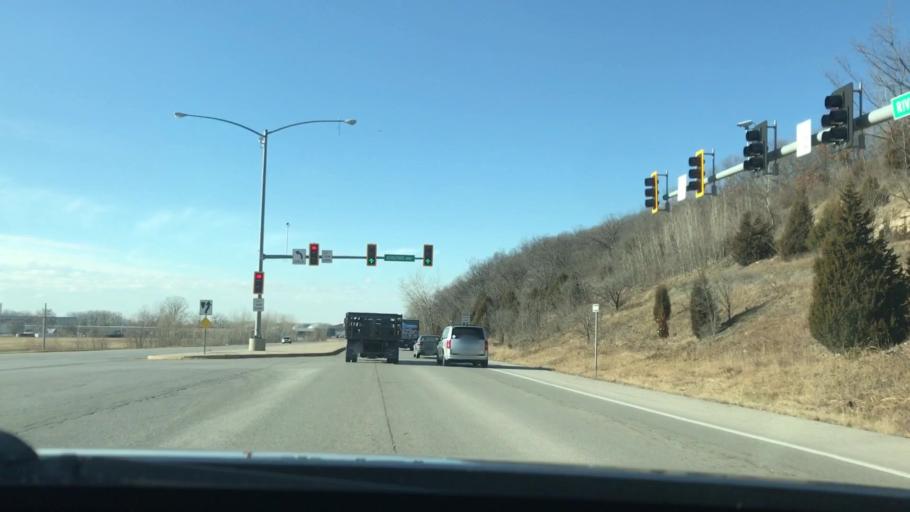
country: US
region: Missouri
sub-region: Platte County
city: Riverside
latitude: 39.1755
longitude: -94.6389
